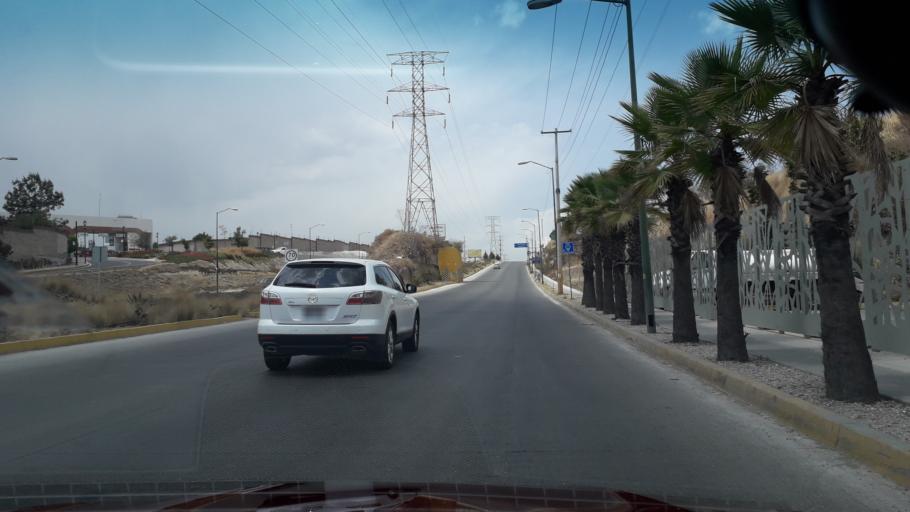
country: MX
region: Puebla
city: Tlazcalancingo
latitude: 19.0143
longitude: -98.2469
